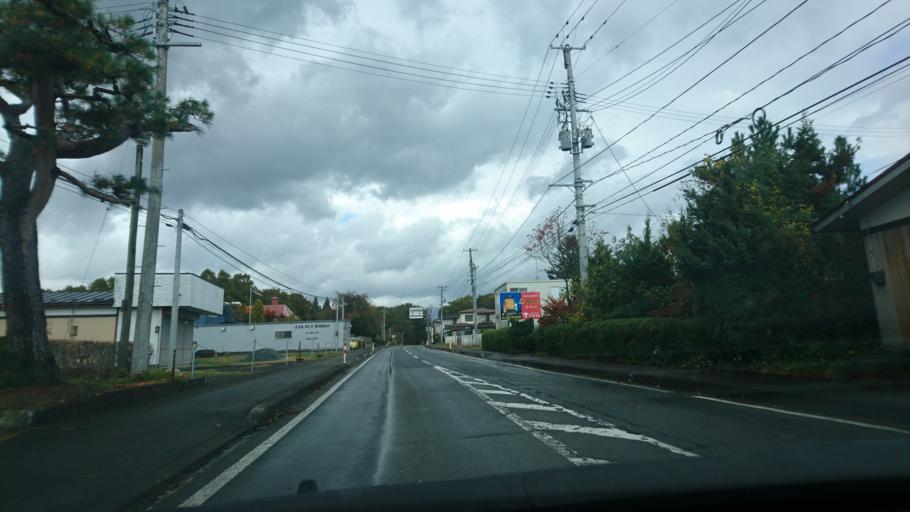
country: JP
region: Iwate
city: Shizukuishi
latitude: 39.6990
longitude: 141.0221
